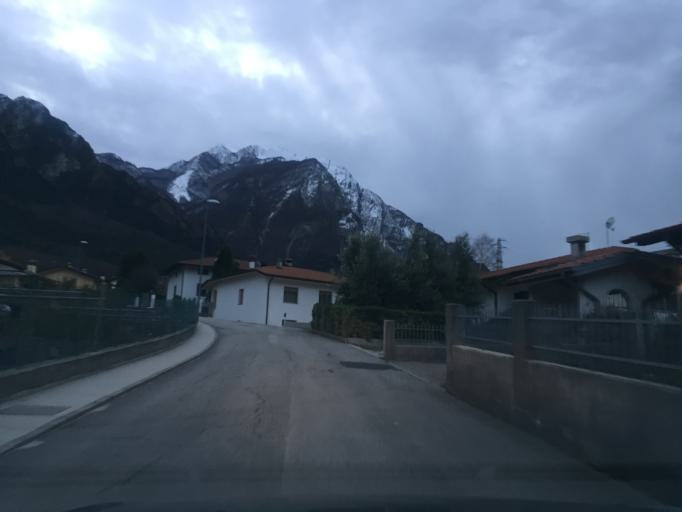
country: IT
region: Friuli Venezia Giulia
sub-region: Provincia di Udine
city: Venzone
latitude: 46.3241
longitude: 13.1373
